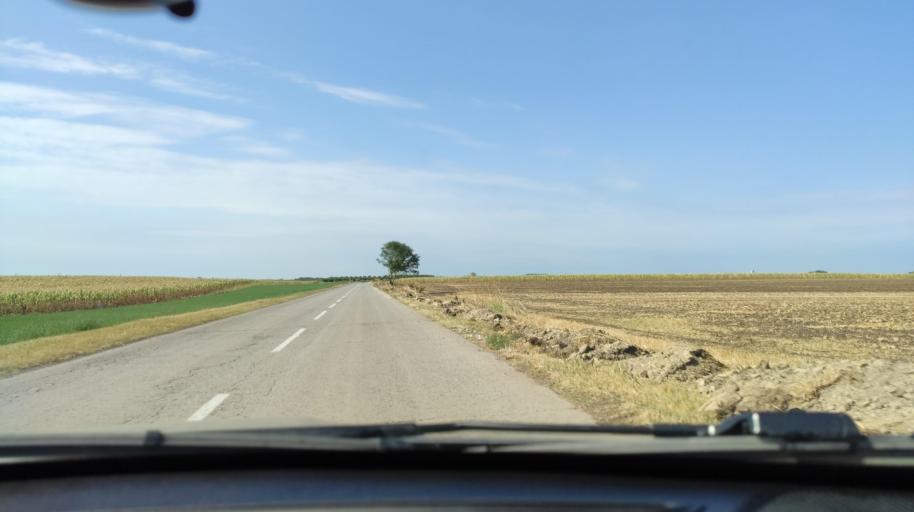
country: RS
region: Autonomna Pokrajina Vojvodina
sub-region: Severnobacki Okrug
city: Backa Topola
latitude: 45.8475
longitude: 19.5610
